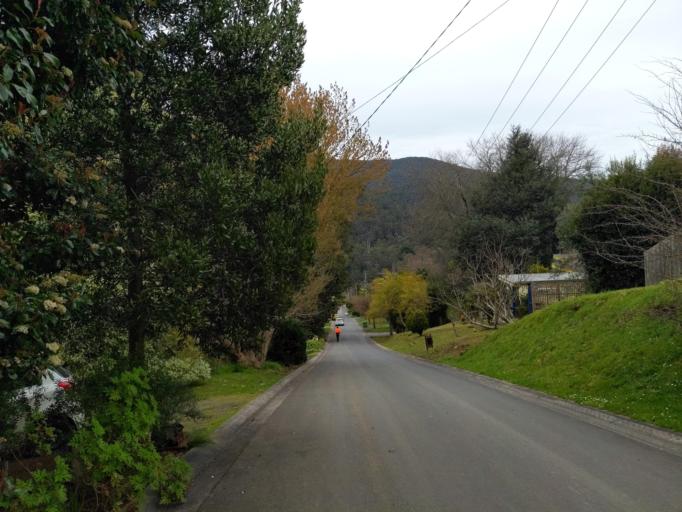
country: AU
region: Victoria
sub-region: Yarra Ranges
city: Millgrove
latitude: -37.7479
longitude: 145.6935
